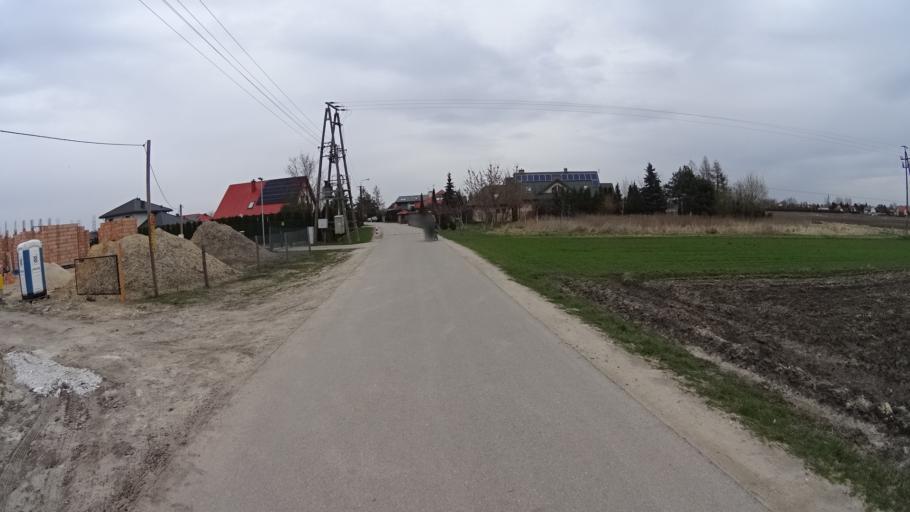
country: PL
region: Masovian Voivodeship
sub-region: Powiat warszawski zachodni
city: Stare Babice
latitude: 52.2456
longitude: 20.8256
